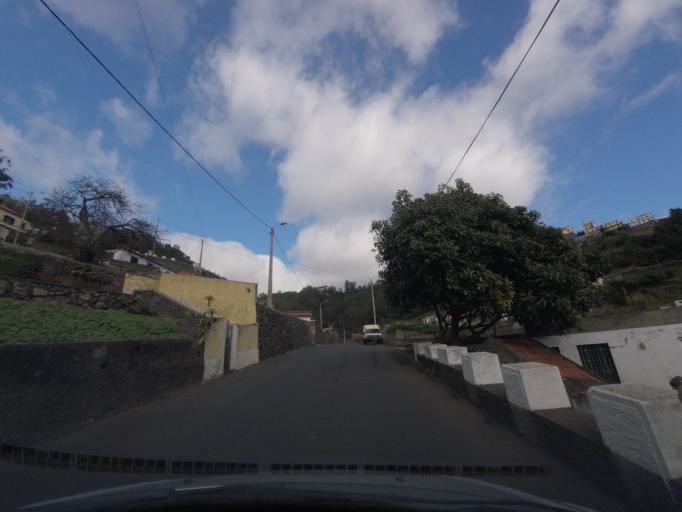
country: PT
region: Madeira
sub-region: Ribeira Brava
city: Campanario
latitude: 32.6649
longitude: -17.0077
